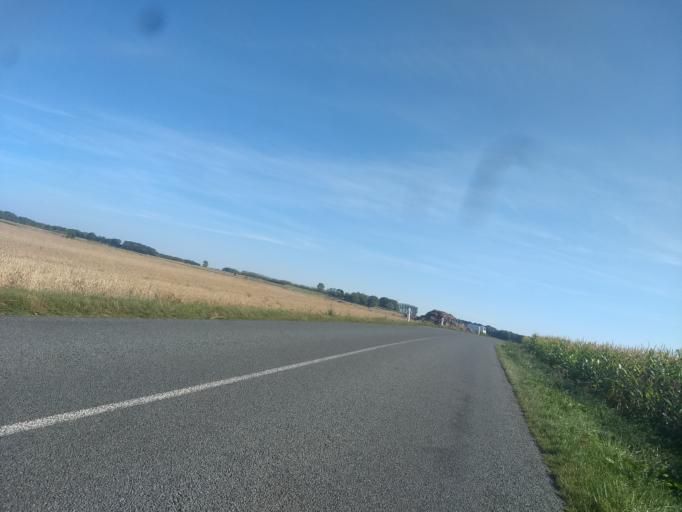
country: FR
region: Nord-Pas-de-Calais
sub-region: Departement du Pas-de-Calais
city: Roeux
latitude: 50.2855
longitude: 2.9019
